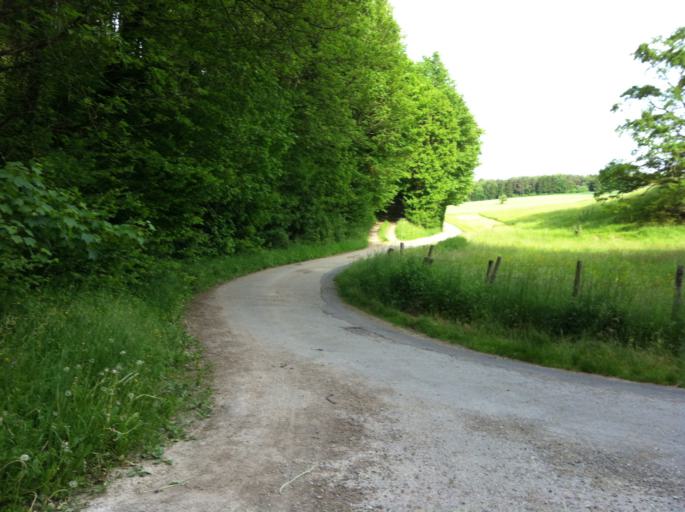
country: DE
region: Baden-Wuerttemberg
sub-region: Freiburg Region
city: Maulburg
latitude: 47.6088
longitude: 7.7931
